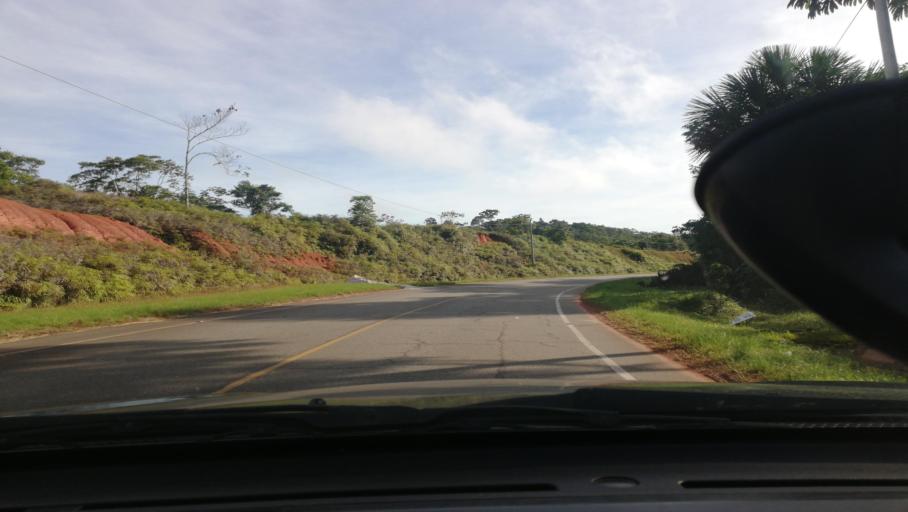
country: PE
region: Loreto
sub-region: Provincia de Loreto
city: Nauta
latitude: -4.4140
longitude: -73.5843
